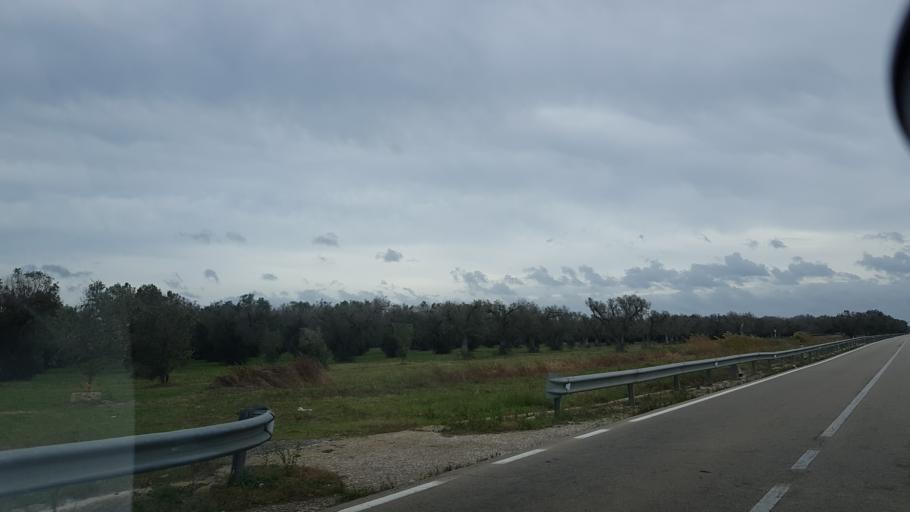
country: IT
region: Apulia
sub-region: Provincia di Brindisi
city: San Pancrazio Salentino
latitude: 40.4077
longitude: 17.8832
